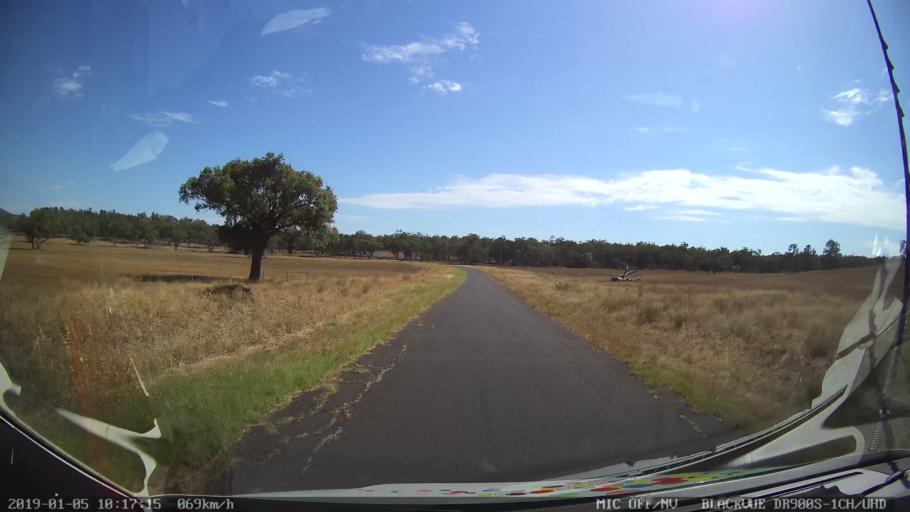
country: AU
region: New South Wales
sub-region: Gilgandra
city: Gilgandra
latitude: -31.5686
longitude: 148.9592
